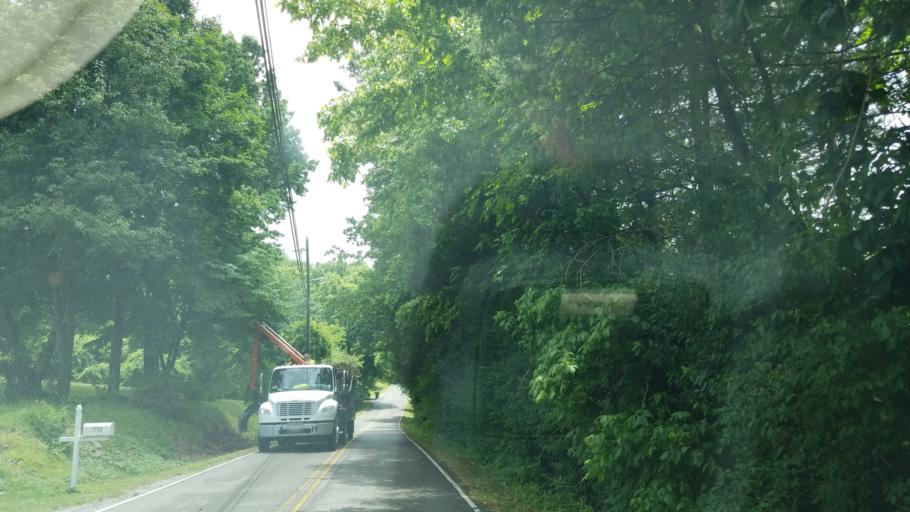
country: US
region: Tennessee
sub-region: Rutherford County
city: La Vergne
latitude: 36.1061
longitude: -86.6495
